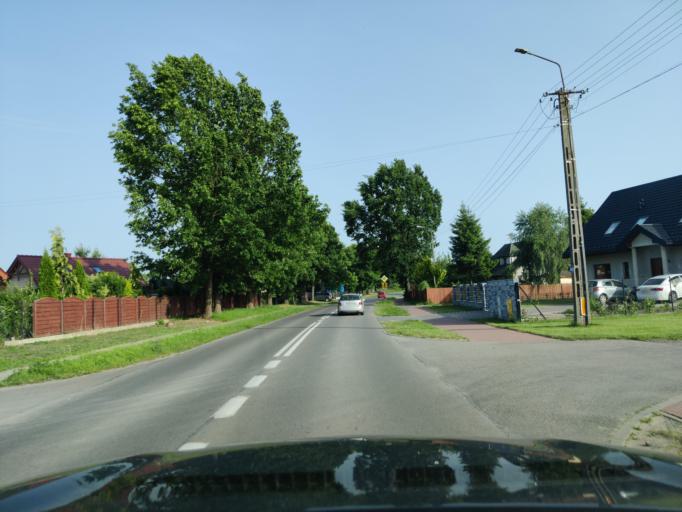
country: PL
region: Masovian Voivodeship
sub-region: Powiat wyszkowski
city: Wyszkow
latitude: 52.6492
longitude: 21.4493
